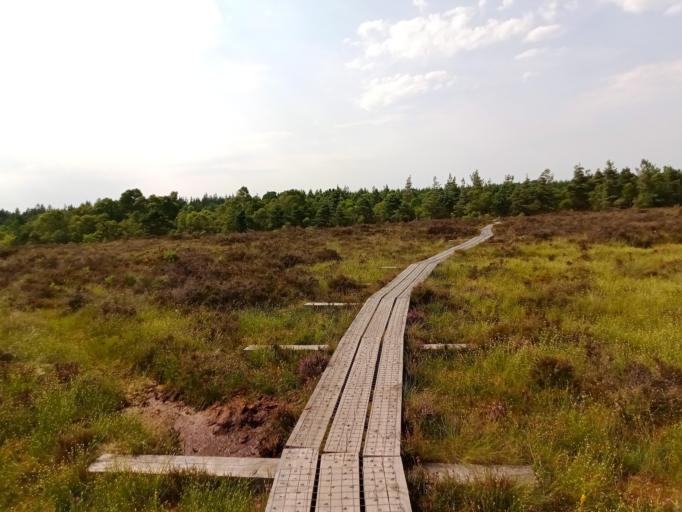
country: IE
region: Leinster
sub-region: Laois
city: Abbeyleix
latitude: 52.8939
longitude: -7.3551
